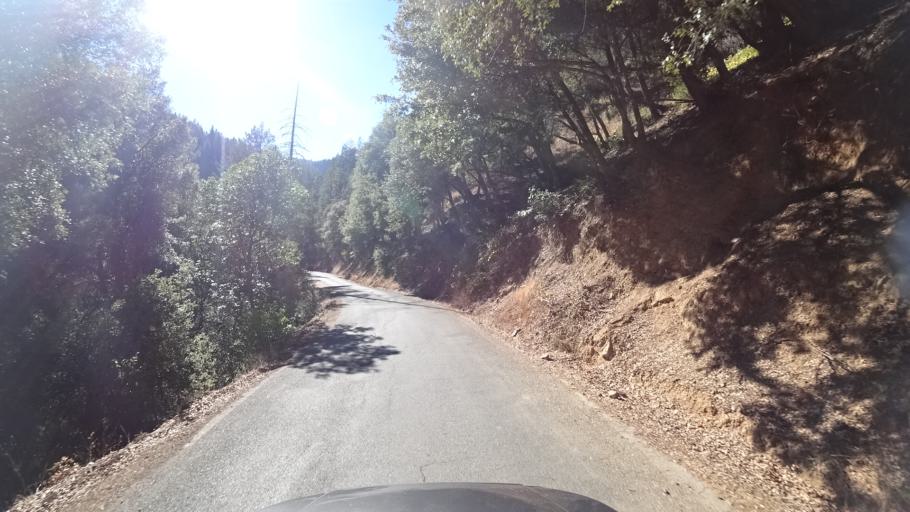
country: US
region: California
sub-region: Siskiyou County
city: Happy Camp
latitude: 41.2956
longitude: -123.1097
